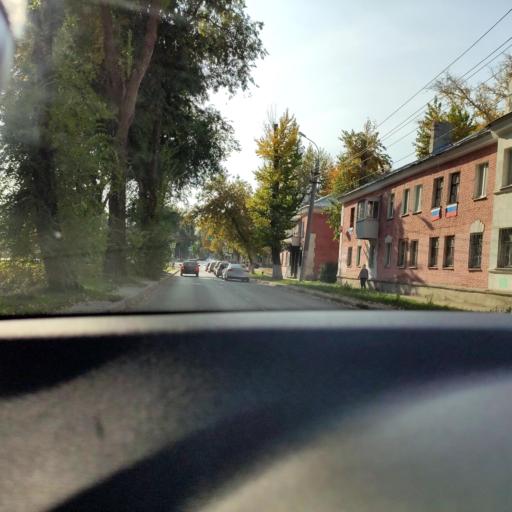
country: RU
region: Samara
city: Samara
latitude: 53.2285
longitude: 50.2531
